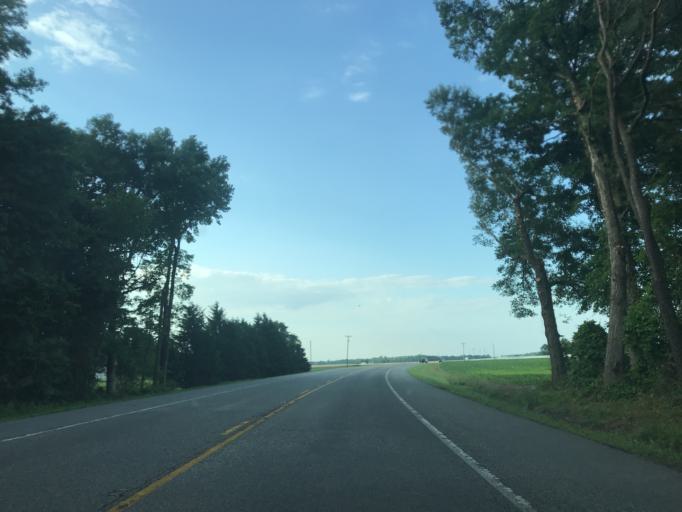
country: US
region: Maryland
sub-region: Caroline County
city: Denton
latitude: 38.8035
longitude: -75.7872
